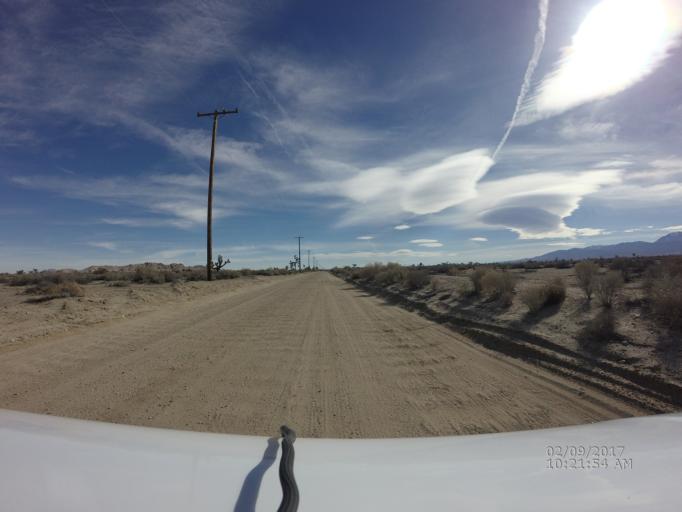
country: US
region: California
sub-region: Los Angeles County
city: Lake Los Angeles
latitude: 34.5726
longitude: -117.9035
